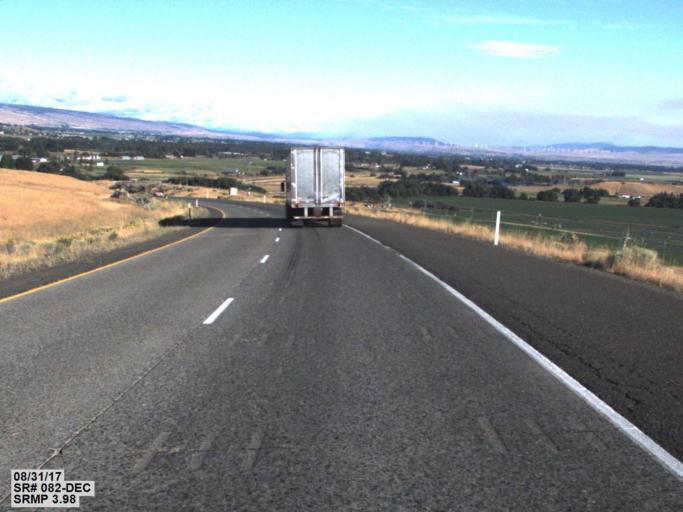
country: US
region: Washington
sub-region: Kittitas County
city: Kittitas
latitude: 46.9197
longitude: -120.4863
